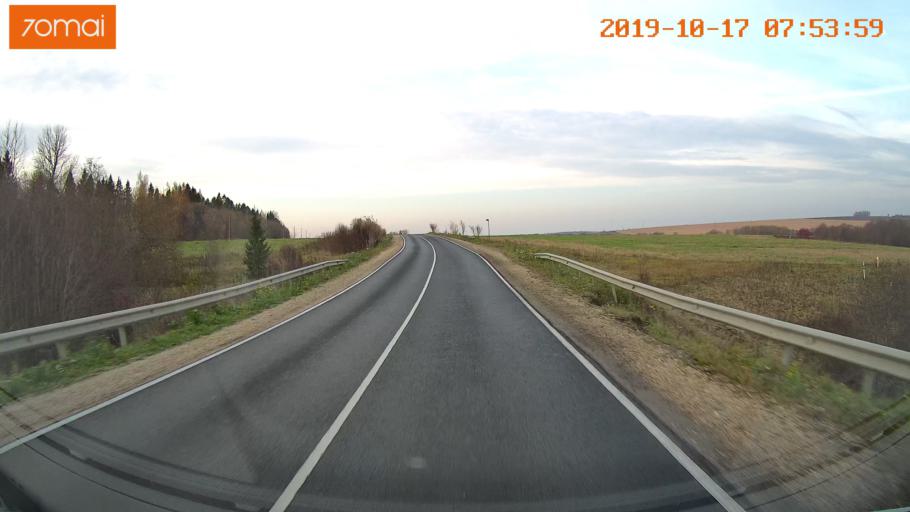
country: RU
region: Vladimir
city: Bavleny
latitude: 56.4555
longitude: 39.6116
